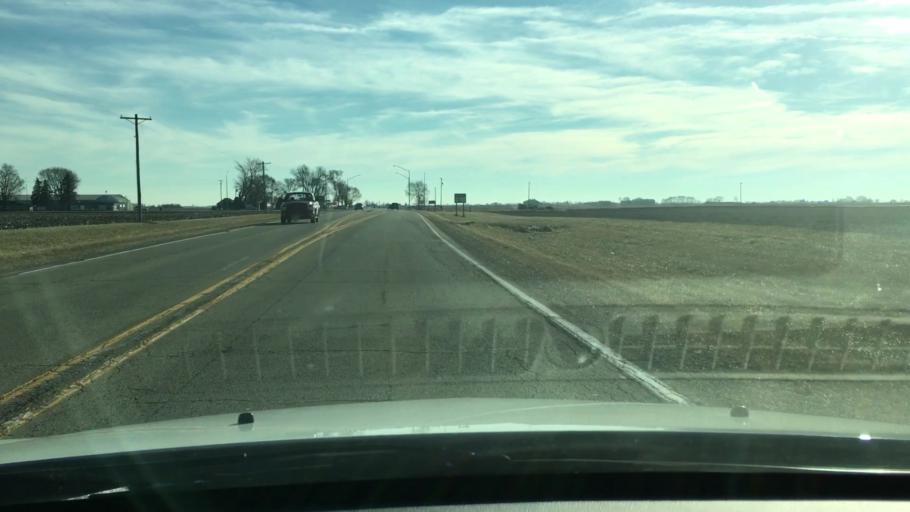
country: US
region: Illinois
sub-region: LaSalle County
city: Mendota
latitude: 41.4722
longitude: -89.1270
